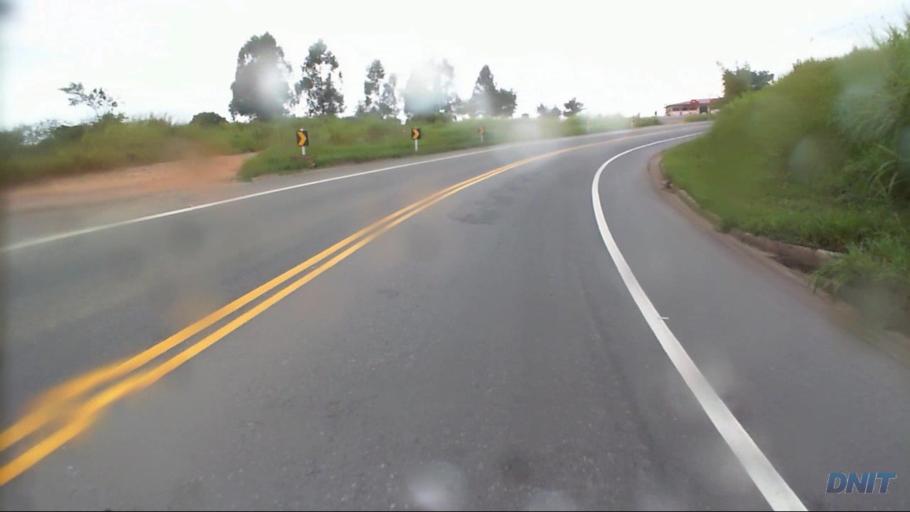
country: BR
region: Minas Gerais
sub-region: Nova Era
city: Nova Era
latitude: -19.6847
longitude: -42.9823
